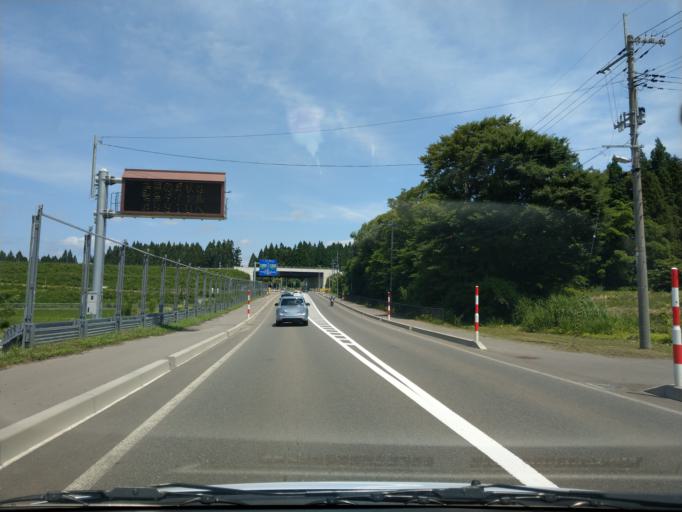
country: JP
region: Akita
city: Takanosu
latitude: 40.1999
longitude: 140.3962
